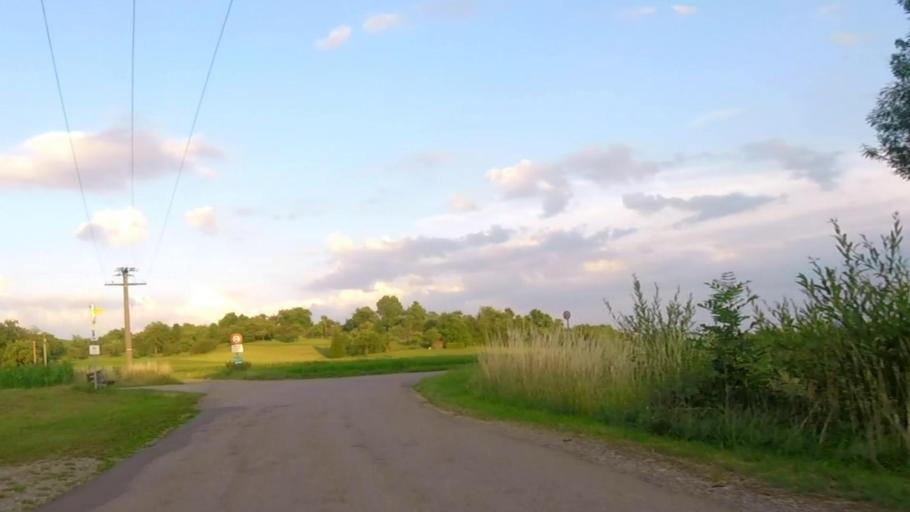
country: DE
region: Baden-Wuerttemberg
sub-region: Regierungsbezirk Stuttgart
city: Oberstenfeld
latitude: 48.9997
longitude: 9.3628
